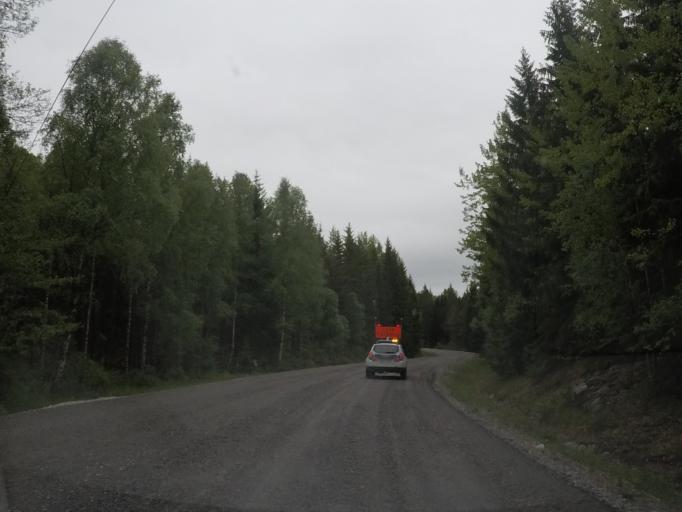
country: SE
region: Soedermanland
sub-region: Flens Kommun
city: Halleforsnas
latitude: 59.2055
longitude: 16.4762
